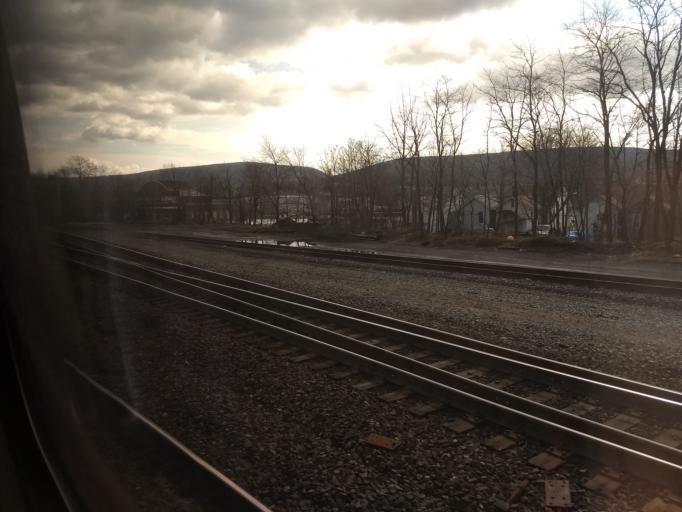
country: US
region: Pennsylvania
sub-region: Blair County
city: Altoona
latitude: 40.5101
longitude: -78.4092
